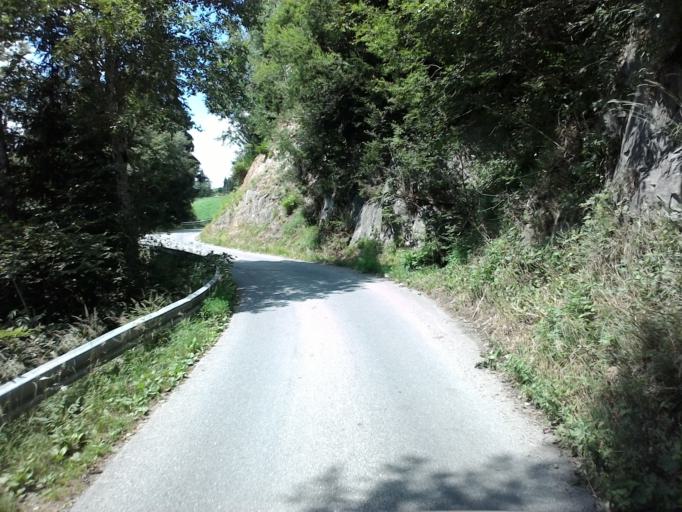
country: AT
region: Tyrol
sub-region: Politischer Bezirk Lienz
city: Untertilliach
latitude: 46.6945
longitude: 12.8054
